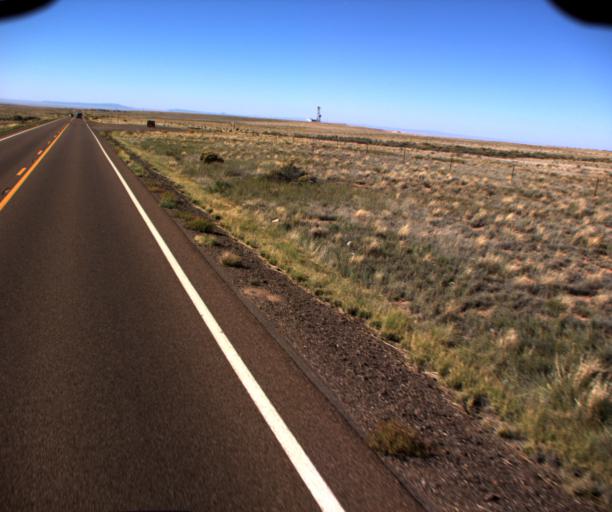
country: US
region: Arizona
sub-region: Navajo County
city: Joseph City
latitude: 35.1531
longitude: -110.4682
